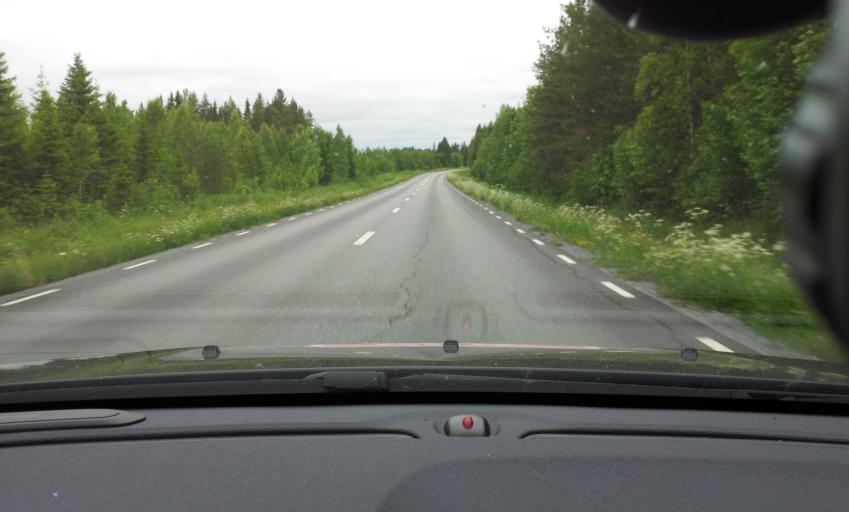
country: SE
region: Jaemtland
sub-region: Bergs Kommun
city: Hoverberg
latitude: 63.0464
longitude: 14.3335
